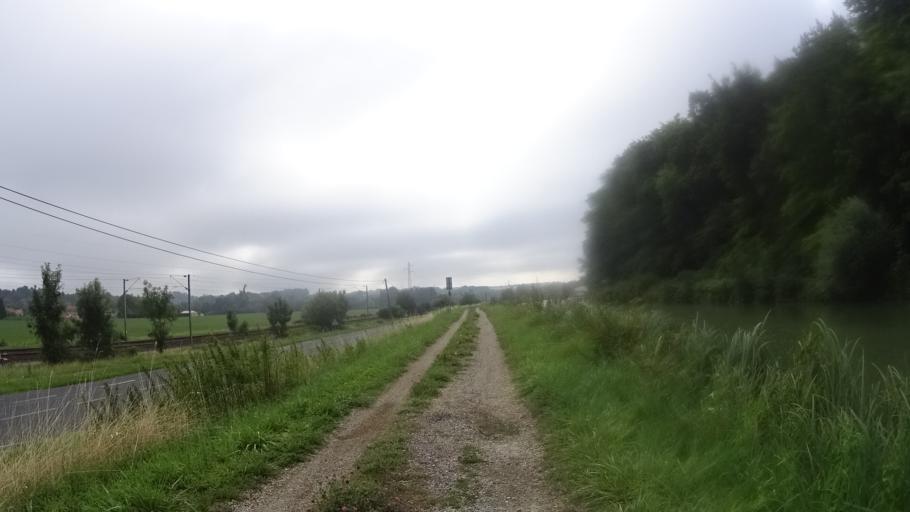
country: FR
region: Lorraine
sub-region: Departement de la Meuse
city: Fains-Veel
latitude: 48.8064
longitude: 5.0973
